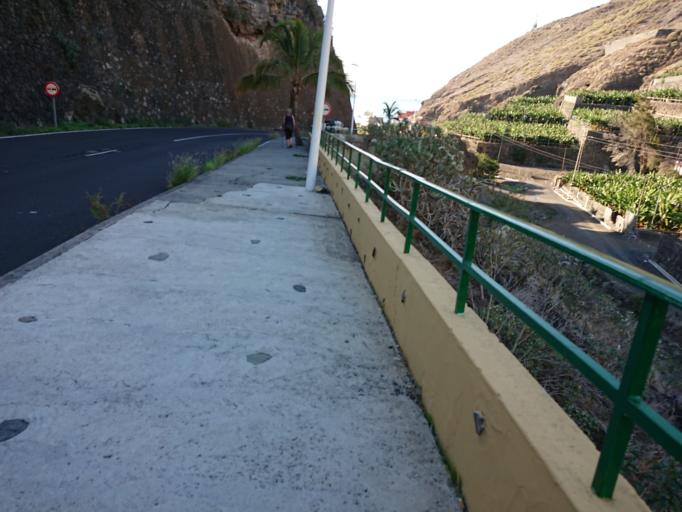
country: ES
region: Canary Islands
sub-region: Provincia de Santa Cruz de Tenerife
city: Tazacorte
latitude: 28.6470
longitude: -17.9391
